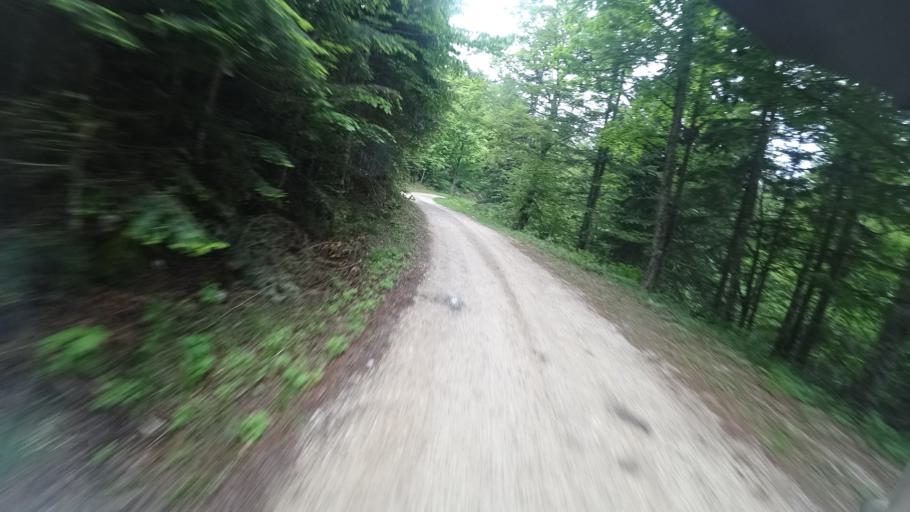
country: BA
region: Federation of Bosnia and Herzegovina
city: Bihac
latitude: 44.6324
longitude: 15.8360
